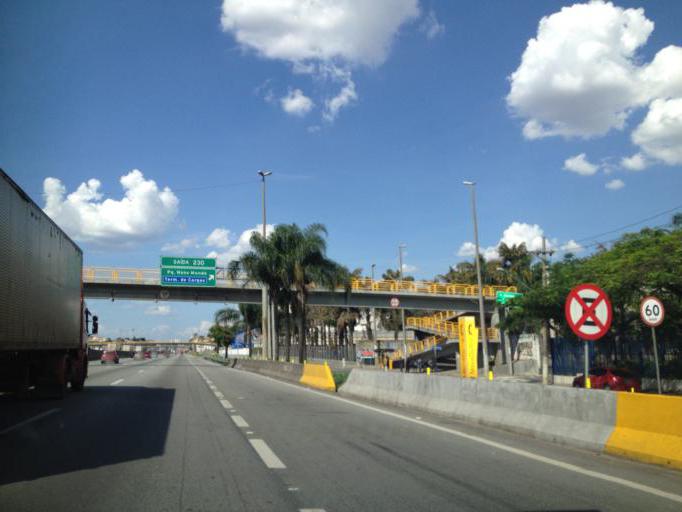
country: BR
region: Sao Paulo
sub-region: Sao Paulo
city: Sao Paulo
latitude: -23.5178
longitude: -46.5807
